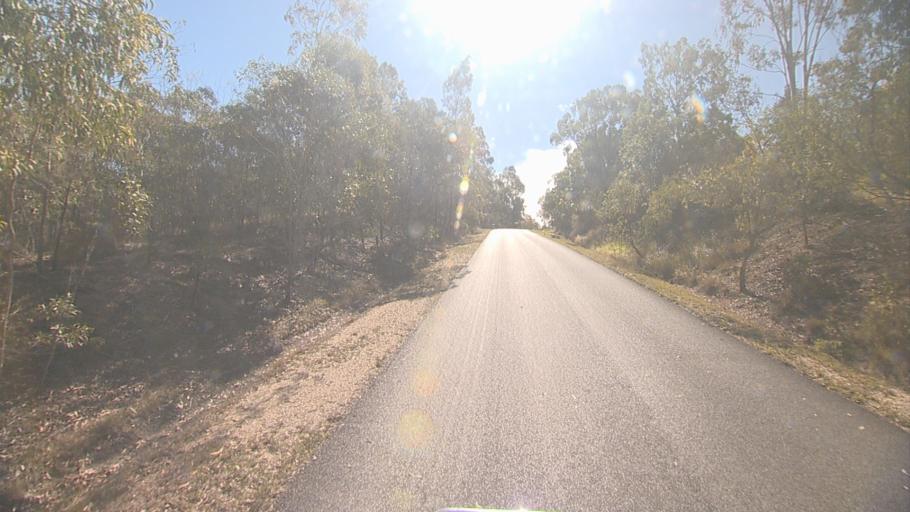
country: AU
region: Queensland
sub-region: Ipswich
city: Springfield Lakes
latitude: -27.7131
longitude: 152.9320
